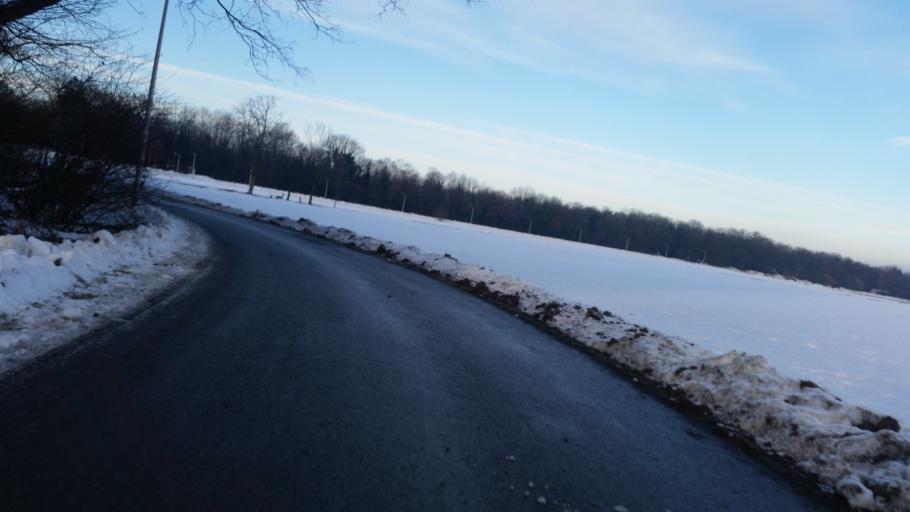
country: AT
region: Vorarlberg
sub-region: Politischer Bezirk Bregenz
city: Hard
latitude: 47.5010
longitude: 9.7078
